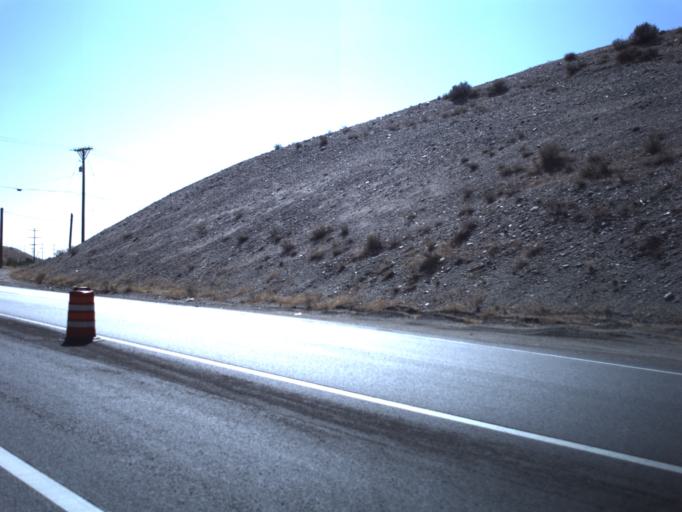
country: US
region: Utah
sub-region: Box Elder County
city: Brigham City
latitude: 41.4964
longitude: -111.9955
